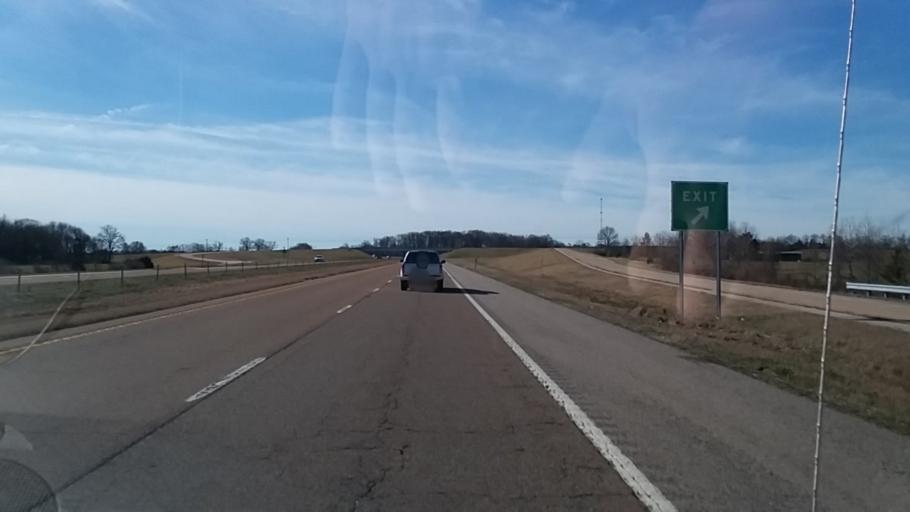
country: US
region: Tennessee
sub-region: Crockett County
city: Alamo
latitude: 35.8021
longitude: -89.1602
